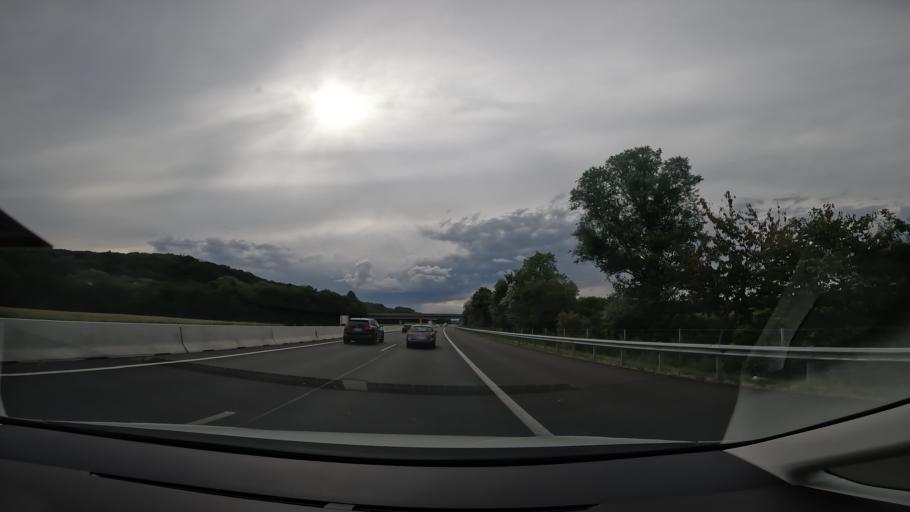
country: AT
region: Styria
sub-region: Politischer Bezirk Hartberg-Fuerstenfeld
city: Ilz
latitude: 47.0780
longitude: 15.9468
